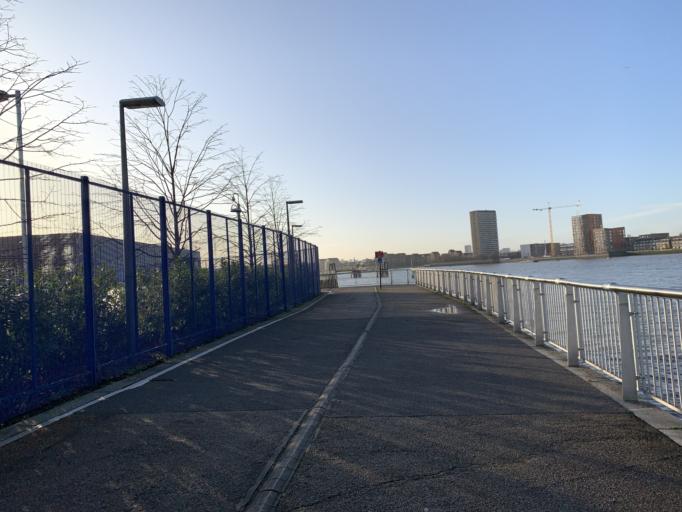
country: GB
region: England
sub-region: Greater London
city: Poplar
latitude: 51.5025
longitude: -0.0017
